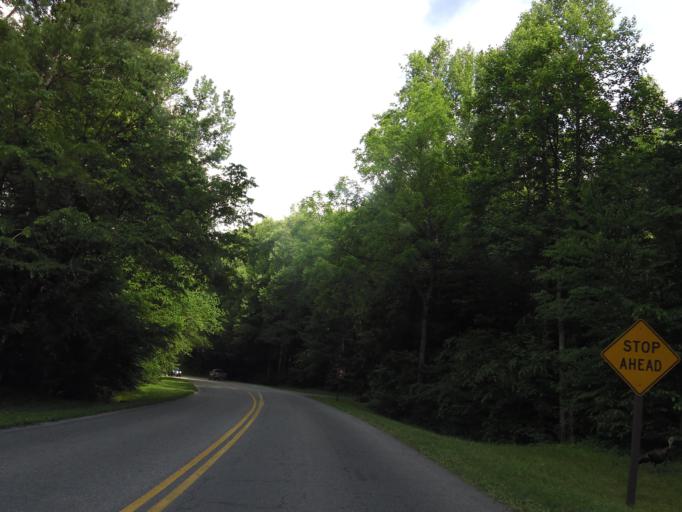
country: US
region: Tennessee
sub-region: Sevier County
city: Gatlinburg
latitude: 35.6848
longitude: -83.5379
